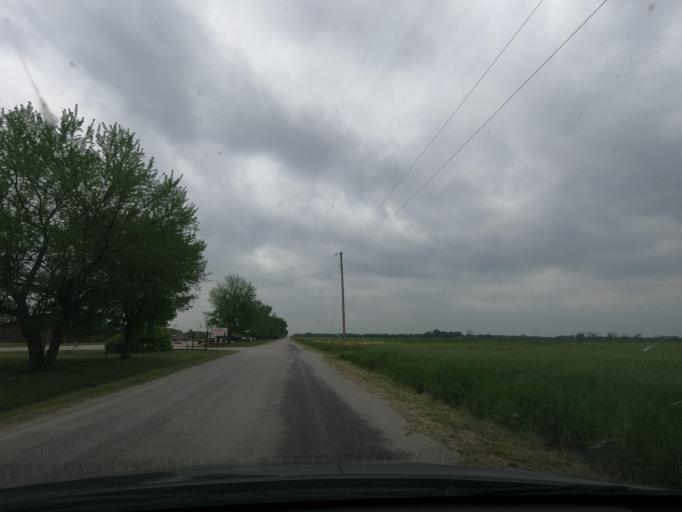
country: US
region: Kansas
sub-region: Cherokee County
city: Columbus
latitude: 37.2747
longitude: -94.9407
